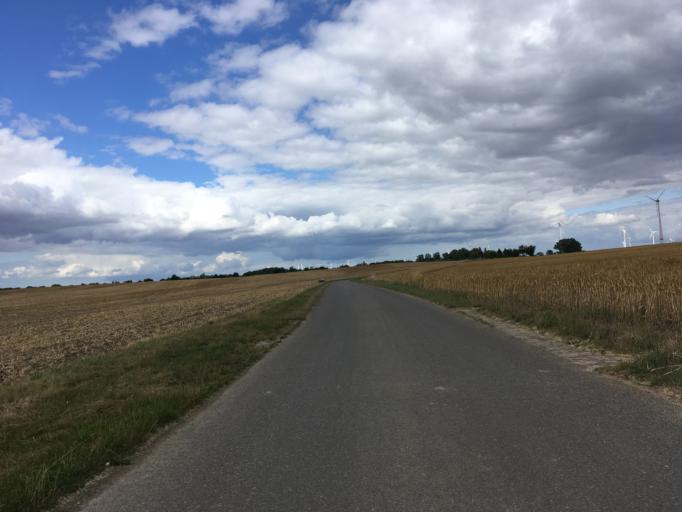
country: DE
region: Brandenburg
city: Gramzow
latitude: 53.2513
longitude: 13.9997
